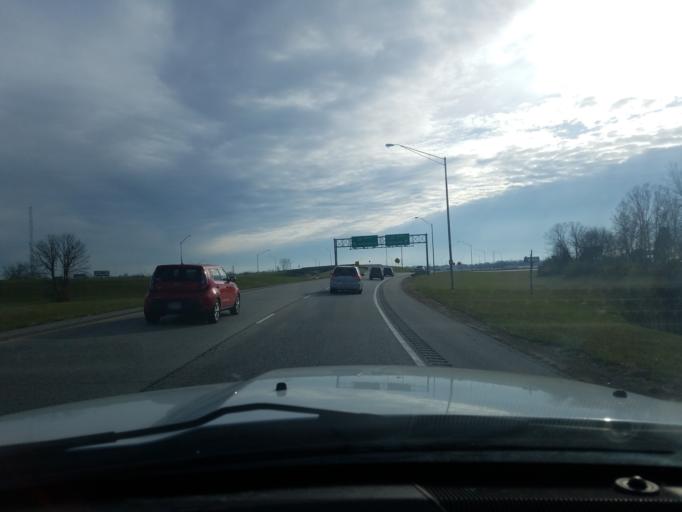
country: US
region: Indiana
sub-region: Clark County
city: Clarksville
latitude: 38.3450
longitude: -85.7577
